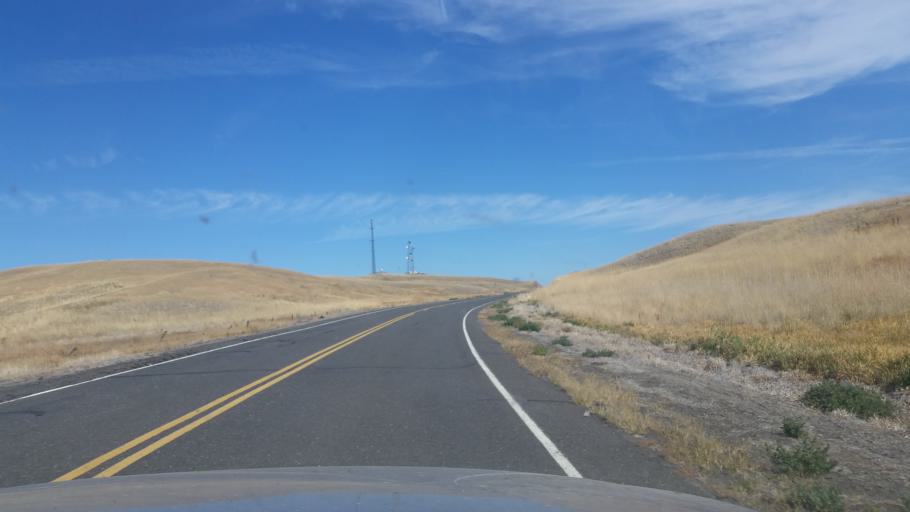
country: US
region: Washington
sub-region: Spokane County
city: Medical Lake
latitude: 47.3725
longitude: -117.8485
